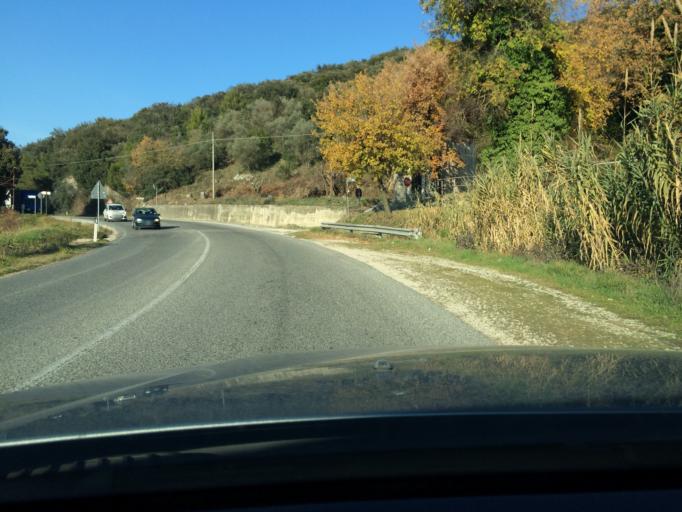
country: IT
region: Umbria
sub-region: Provincia di Terni
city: Fornole
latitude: 42.5538
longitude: 12.4425
